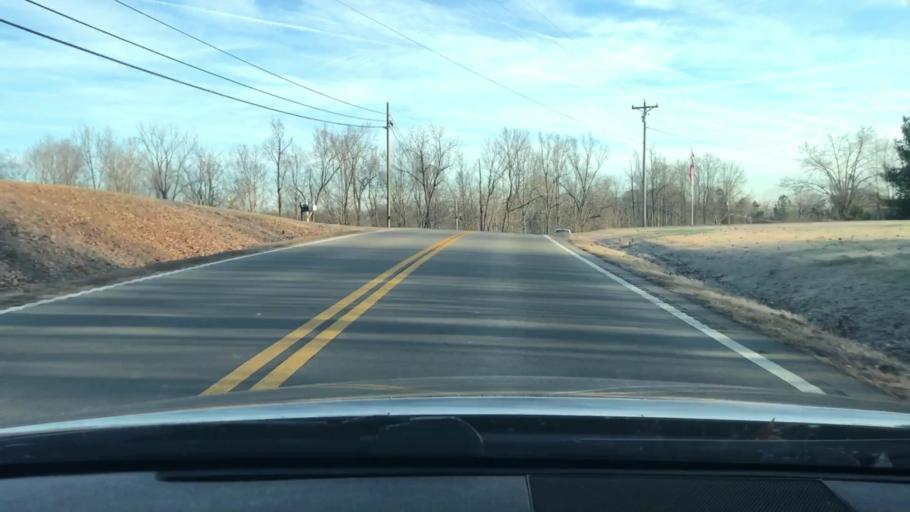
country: US
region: Tennessee
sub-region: Cheatham County
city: Ashland City
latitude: 36.2782
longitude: -87.1166
